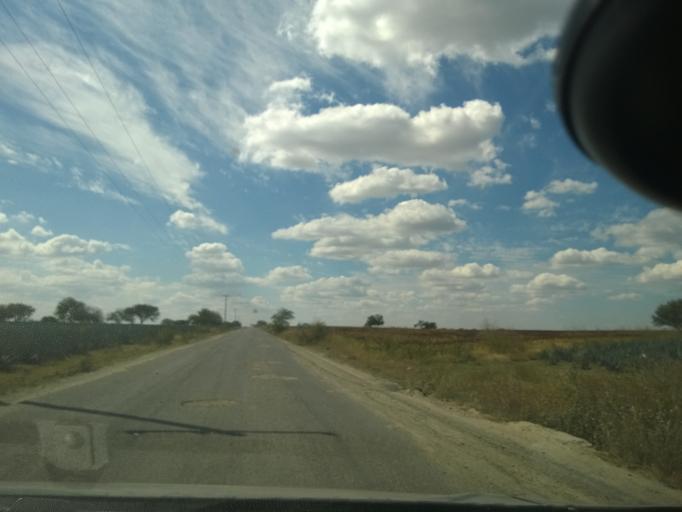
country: MX
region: Guanajuato
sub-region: Leon
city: Plan Guanajuato (La Sandia)
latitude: 20.8656
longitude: -101.6177
